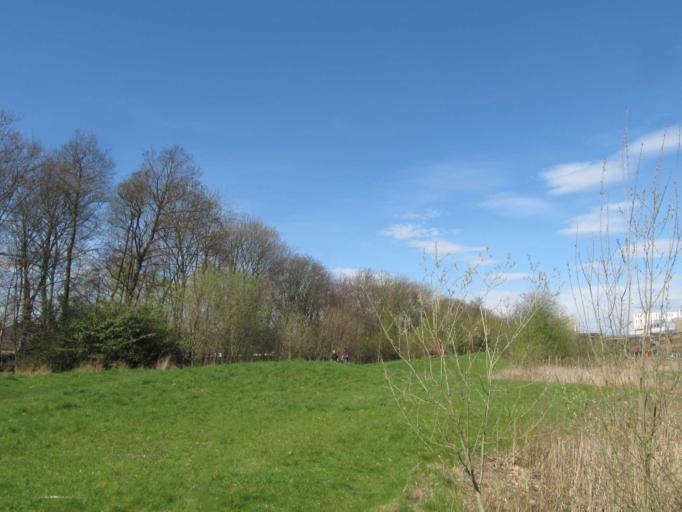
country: GB
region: England
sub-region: Nottingham
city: Nottingham
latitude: 52.9508
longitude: -1.1873
